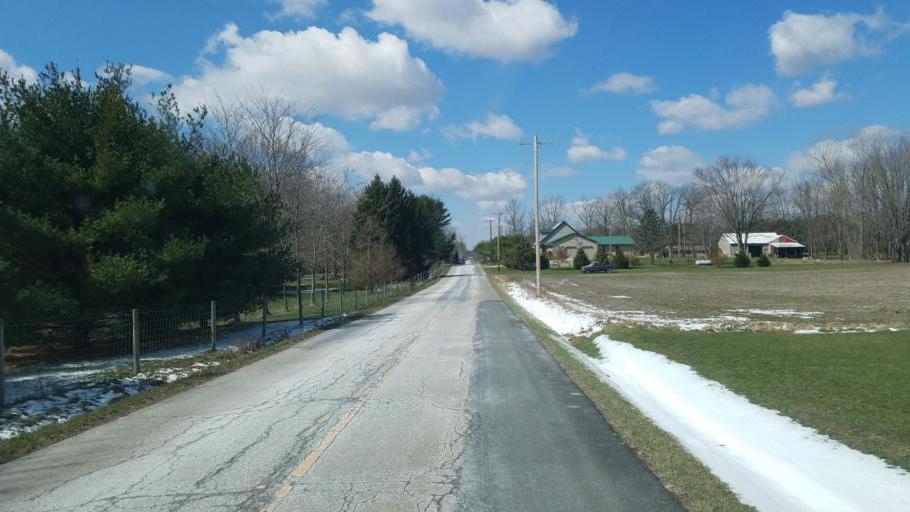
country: US
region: Ohio
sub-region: Knox County
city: Mount Vernon
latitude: 40.3140
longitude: -82.5471
